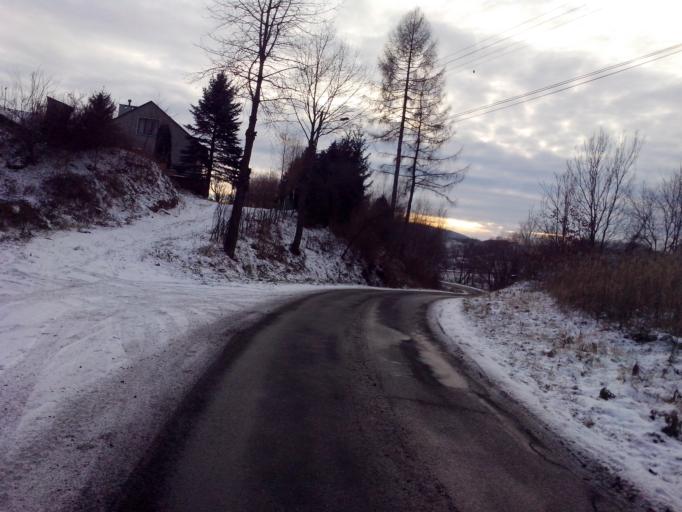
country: PL
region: Subcarpathian Voivodeship
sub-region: Powiat strzyzowski
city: Strzyzow
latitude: 49.8607
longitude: 21.7999
